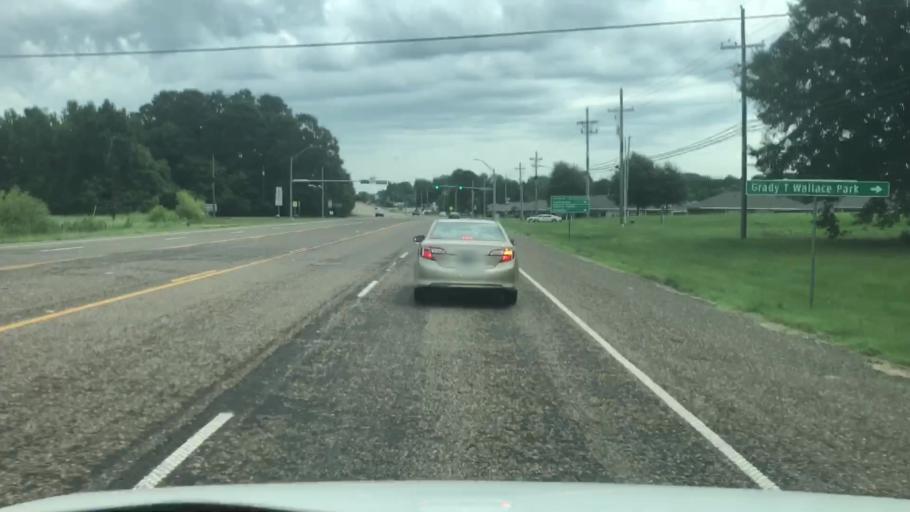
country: US
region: Texas
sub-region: Bowie County
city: Wake Village
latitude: 33.3963
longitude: -94.0935
